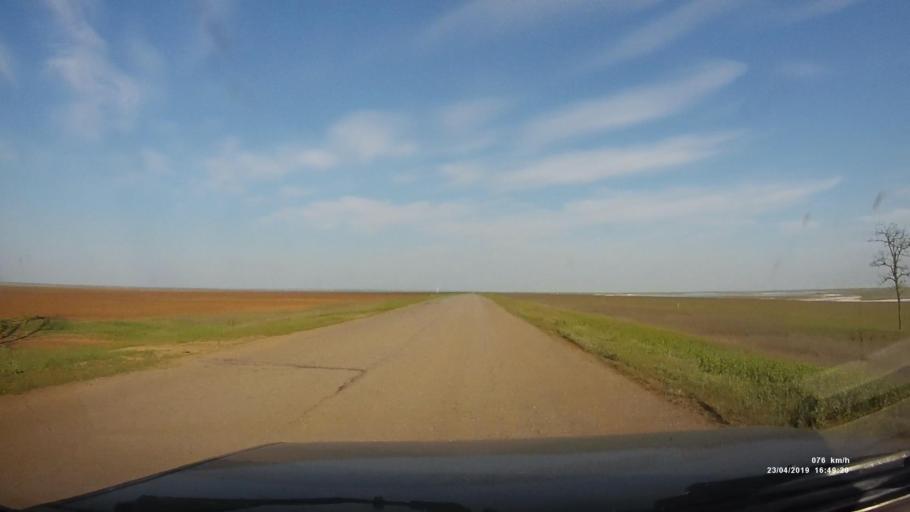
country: RU
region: Kalmykiya
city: Priyutnoye
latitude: 46.3314
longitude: 43.2752
